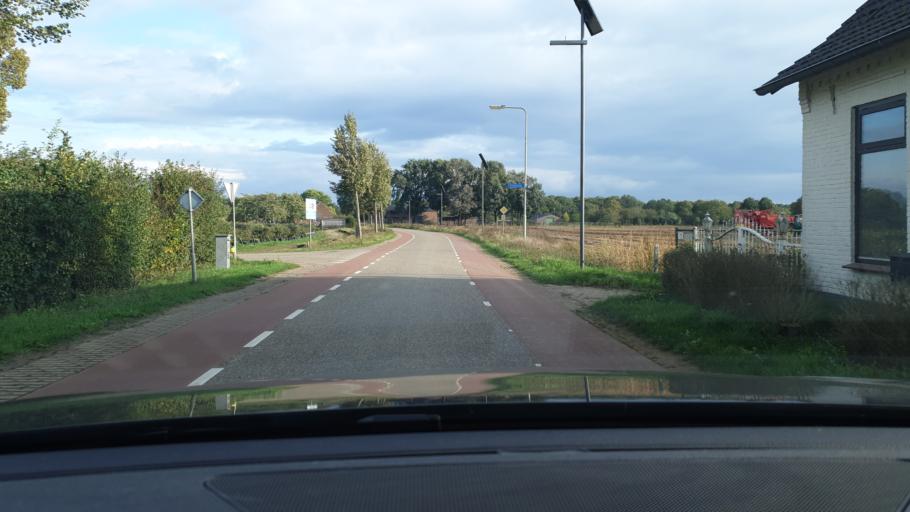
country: NL
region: Limburg
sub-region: Gemeente Bergen
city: Wellerlooi
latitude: 51.4944
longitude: 6.1420
